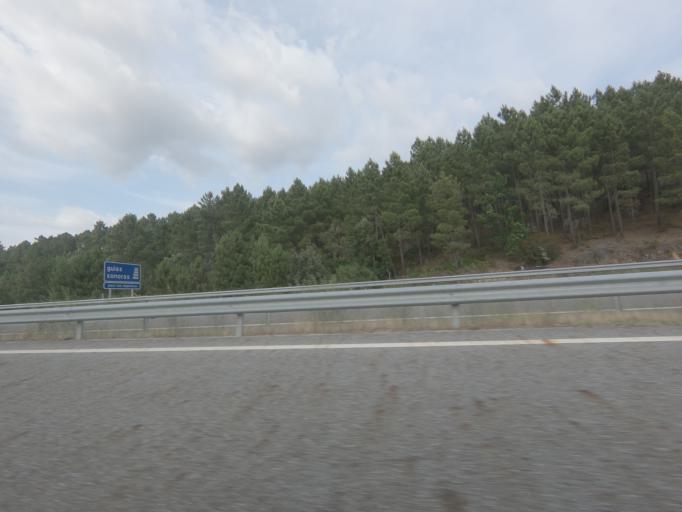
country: PT
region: Vila Real
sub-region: Boticas
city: Boticas
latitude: 41.6766
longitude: -7.5664
